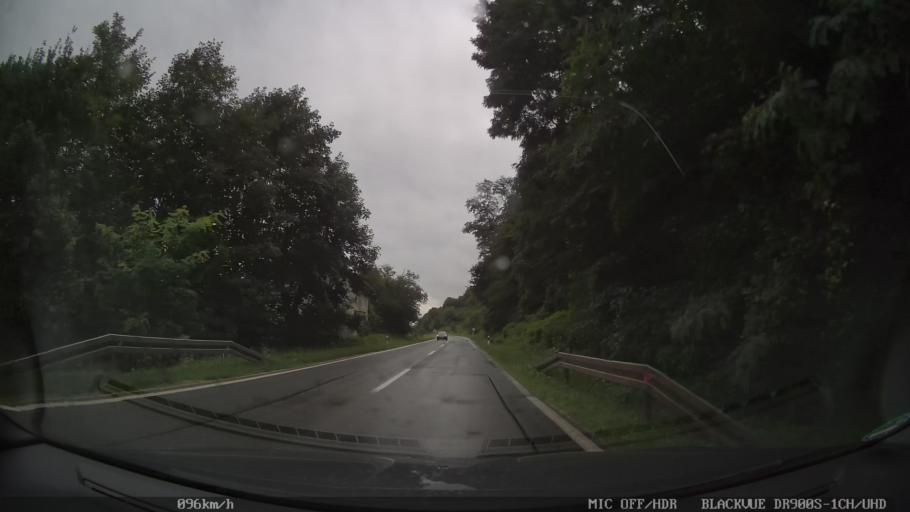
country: HR
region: Licko-Senjska
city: Brinje
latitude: 44.9562
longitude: 15.0980
